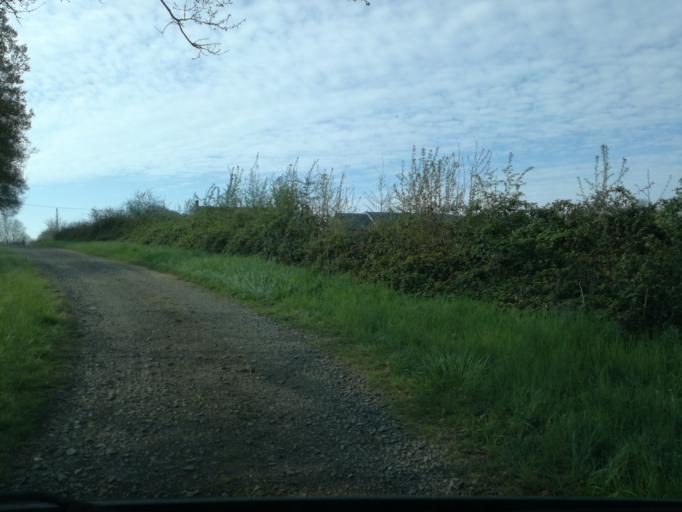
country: FR
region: Pays de la Loire
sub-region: Departement de la Sarthe
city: Brulon
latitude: 48.0544
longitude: -0.2482
